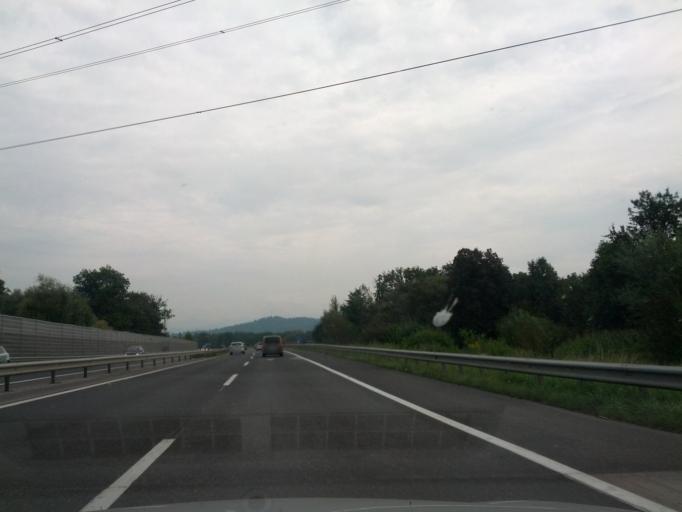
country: SI
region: Dol pri Ljubljani
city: Dol pri Ljubljani
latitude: 46.1018
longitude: 14.5945
